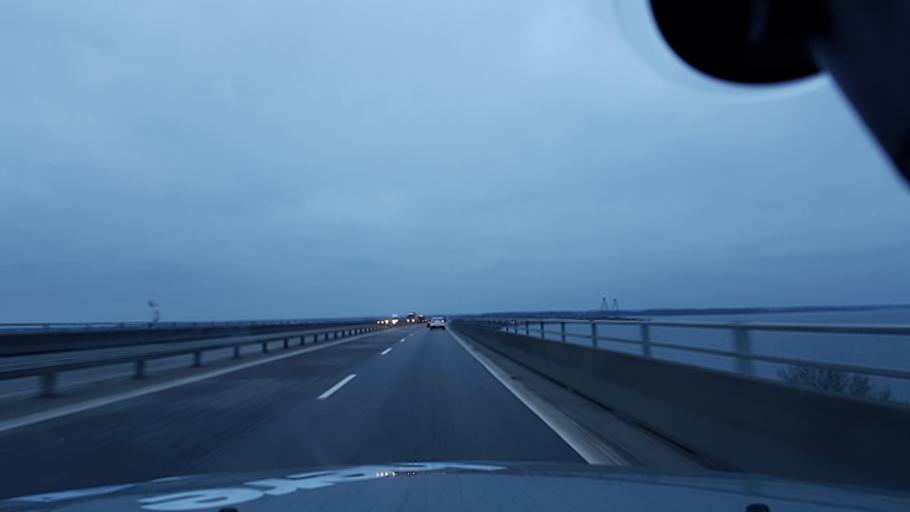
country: DK
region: Zealand
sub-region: Vordingborg Kommune
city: Nyrad
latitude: 54.9693
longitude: 12.0023
